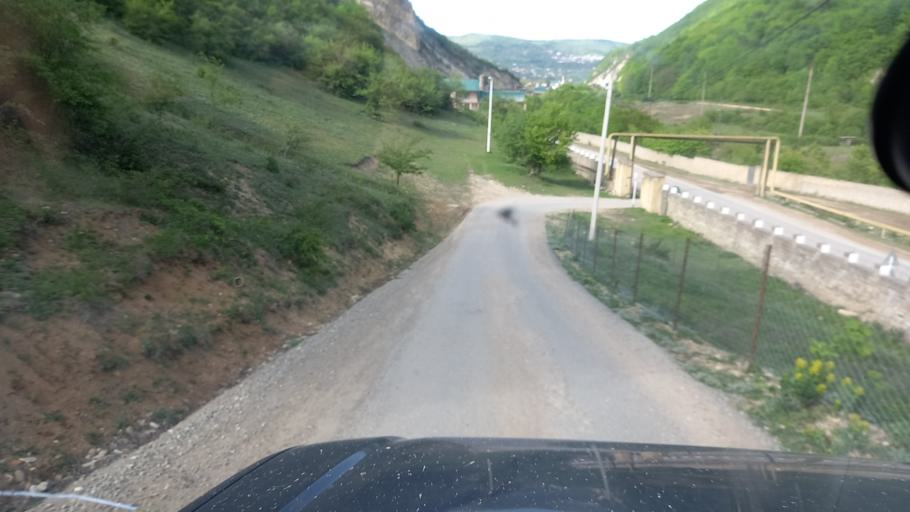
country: RU
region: Dagestan
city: Khuchni
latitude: 41.9649
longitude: 47.9588
